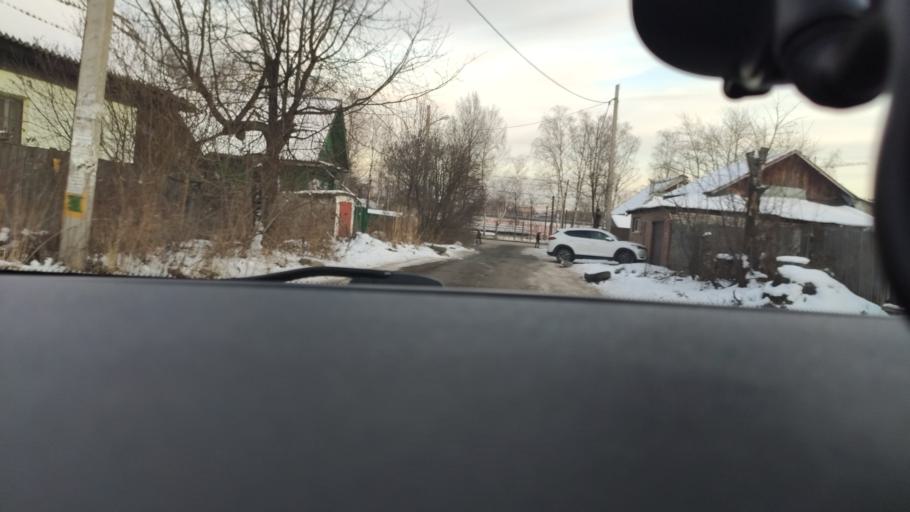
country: RU
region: Perm
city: Perm
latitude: 58.1111
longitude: 56.2953
